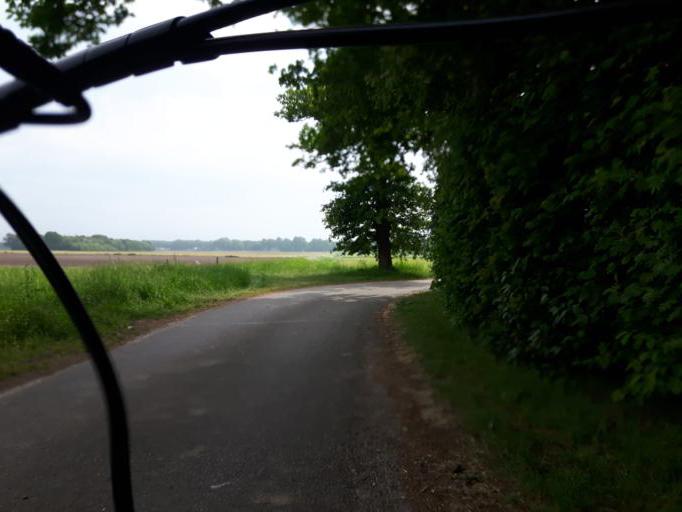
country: NL
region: North Brabant
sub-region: Gemeente Bergen op Zoom
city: Lepelstraat
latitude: 51.5379
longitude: 4.3132
